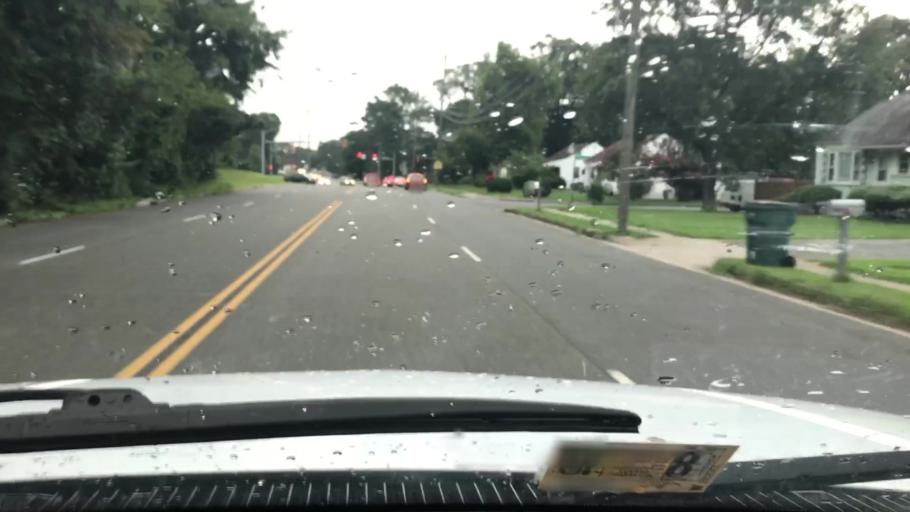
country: US
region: Virginia
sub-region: Henrico County
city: Dumbarton
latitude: 37.6010
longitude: -77.5052
